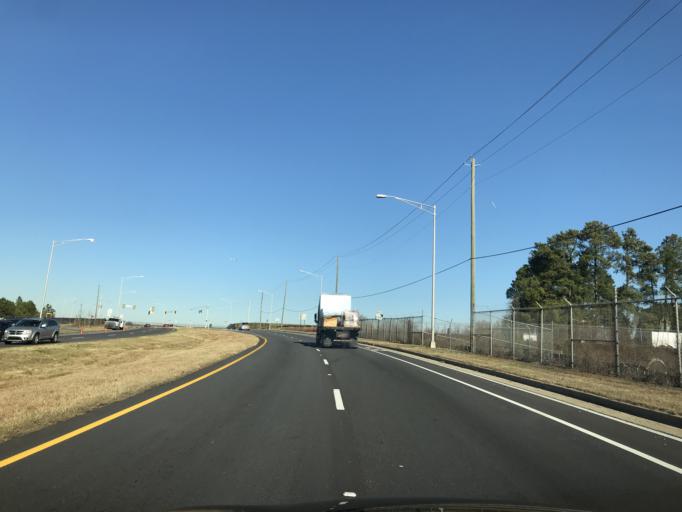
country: US
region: Georgia
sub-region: Fulton County
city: College Park
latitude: 33.6268
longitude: -84.4464
